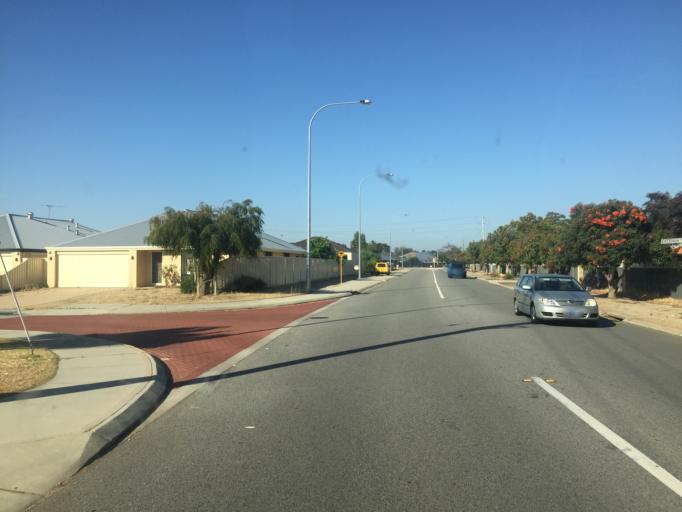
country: AU
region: Western Australia
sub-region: Canning
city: East Cannington
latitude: -32.0032
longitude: 115.9810
